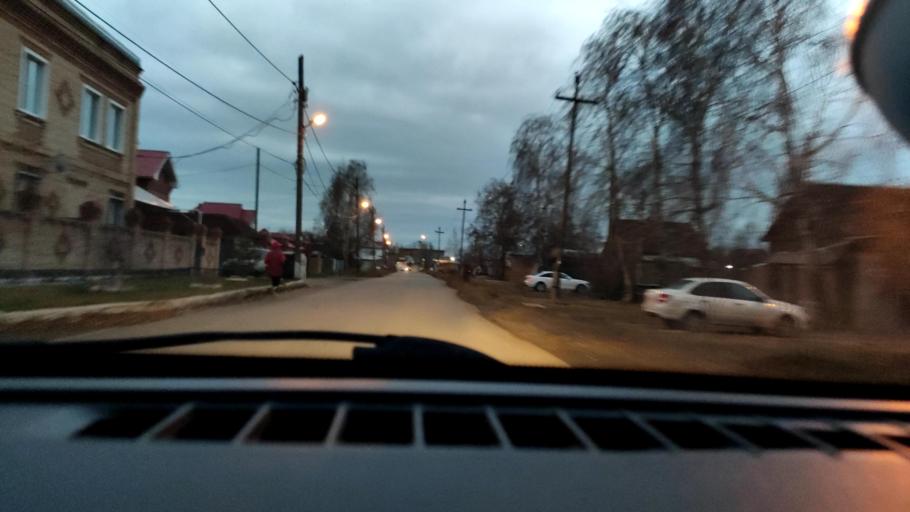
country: RU
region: Samara
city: Smyshlyayevka
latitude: 53.2425
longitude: 50.3275
